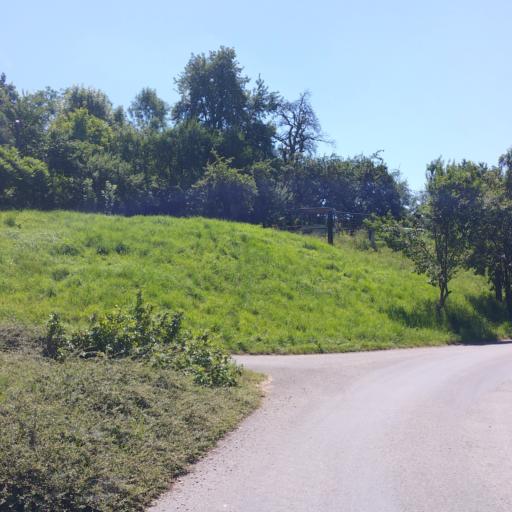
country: AT
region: Styria
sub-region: Politischer Bezirk Leibnitz
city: Gleinstatten
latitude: 46.7342
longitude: 15.3512
